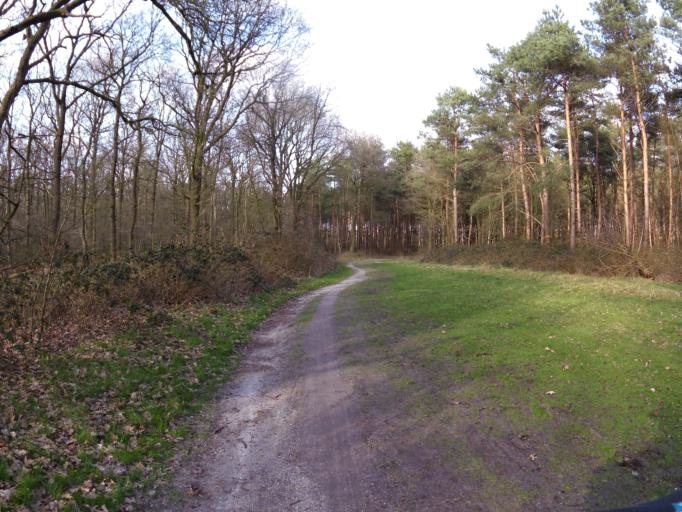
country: NL
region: Overijssel
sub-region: Gemeente Steenwijkerland
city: Steenwijk
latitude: 52.8035
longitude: 6.1133
